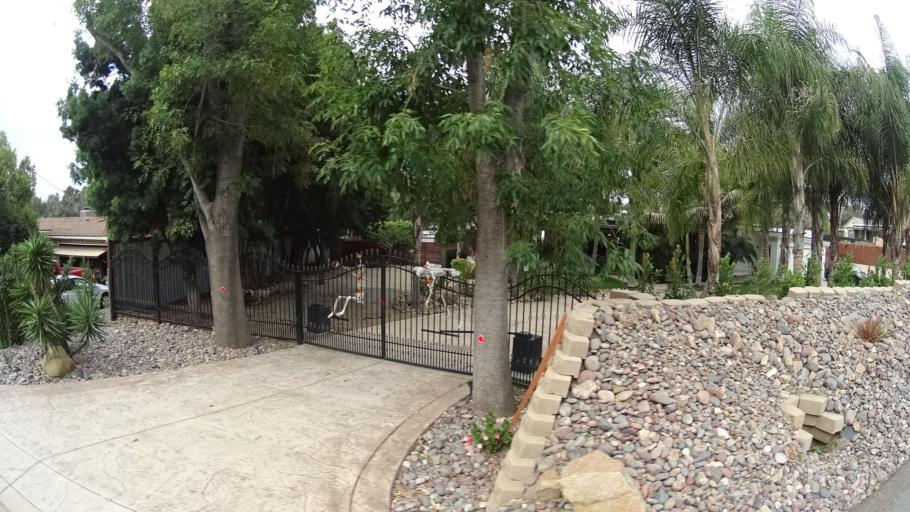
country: US
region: California
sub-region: San Diego County
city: Spring Valley
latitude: 32.7572
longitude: -116.9990
